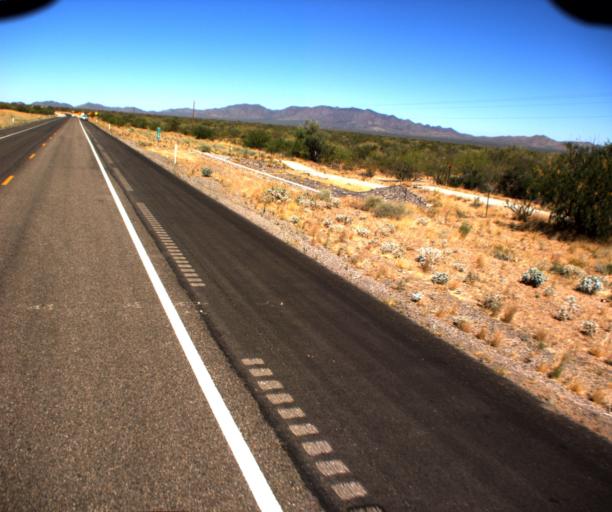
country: US
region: Arizona
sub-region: Pima County
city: Sells
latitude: 32.0095
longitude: -111.6659
